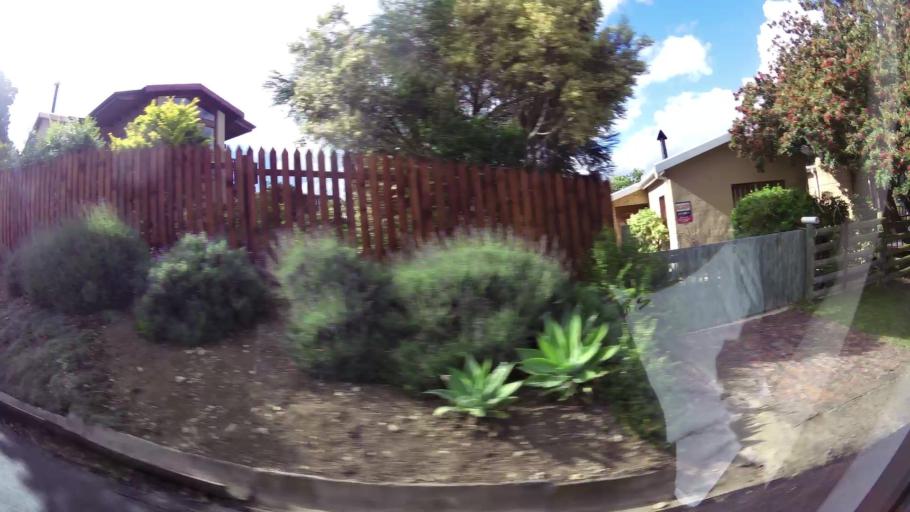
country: ZA
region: Western Cape
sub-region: Eden District Municipality
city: Knysna
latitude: -34.0541
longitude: 23.0842
